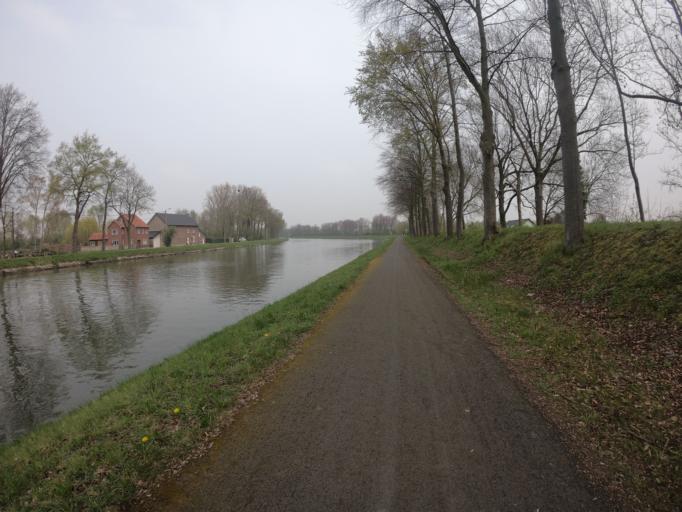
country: BE
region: Flanders
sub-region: Provincie Limburg
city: Maasmechelen
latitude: 50.9262
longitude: 5.7106
